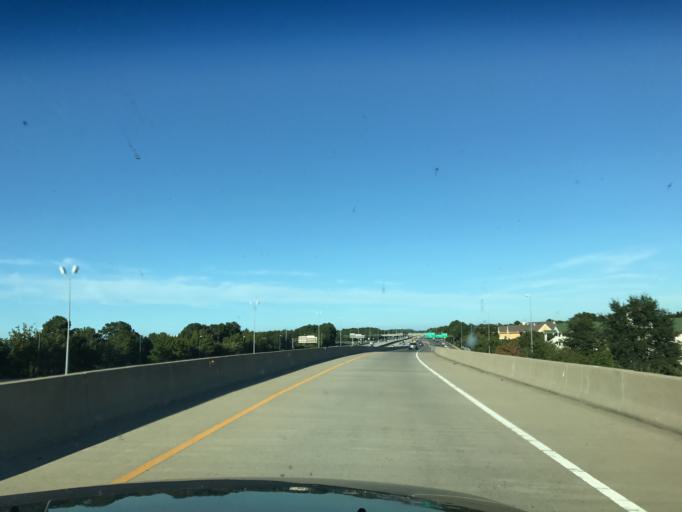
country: US
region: Virginia
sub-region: City of Chesapeake
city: Chesapeake
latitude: 36.7796
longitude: -76.2430
